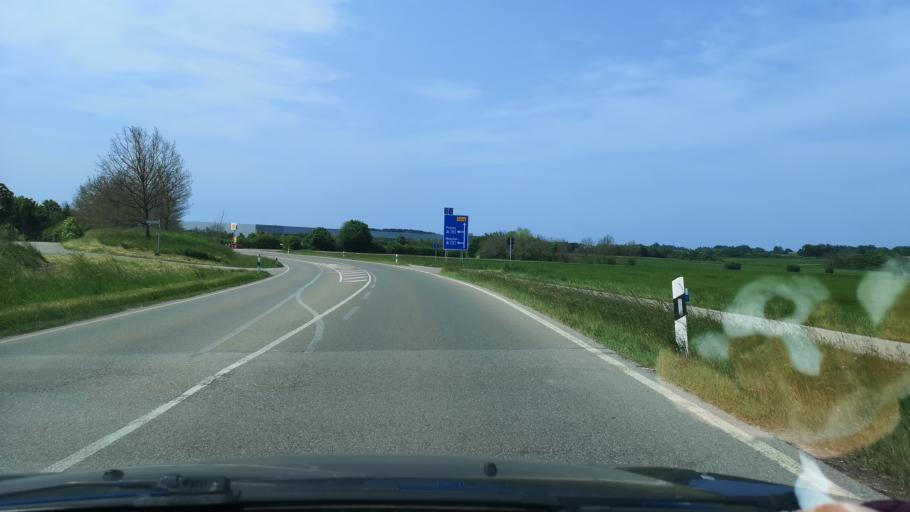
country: DE
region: Bavaria
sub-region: Upper Bavaria
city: Anzing
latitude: 48.1644
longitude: 11.8572
